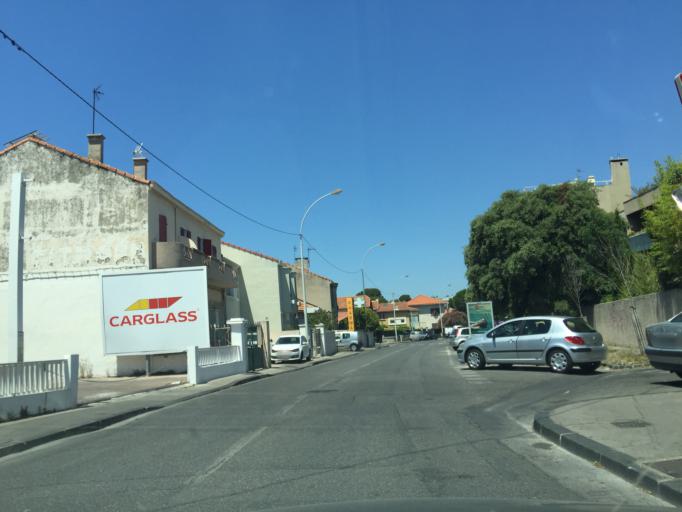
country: FR
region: Provence-Alpes-Cote d'Azur
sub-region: Departement des Bouches-du-Rhone
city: Marseille 09
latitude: 43.2506
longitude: 5.3954
